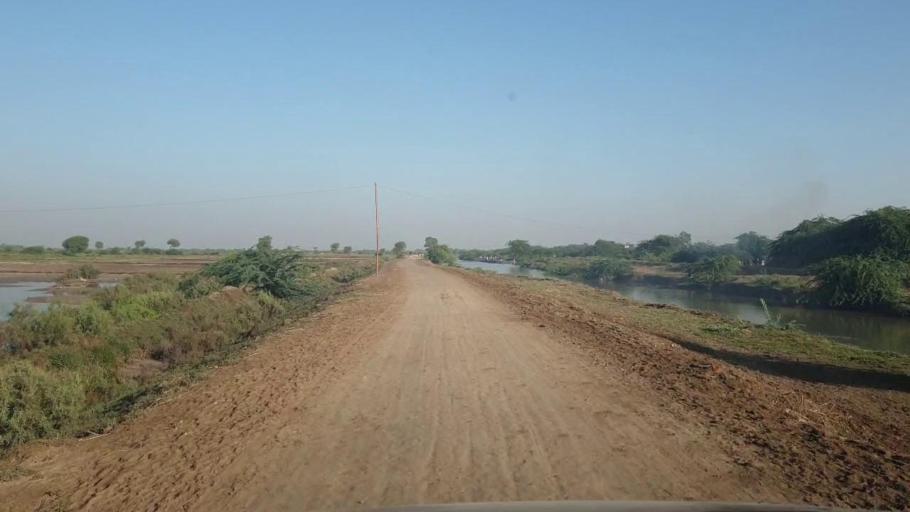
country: PK
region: Sindh
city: Badin
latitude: 24.6797
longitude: 68.8168
